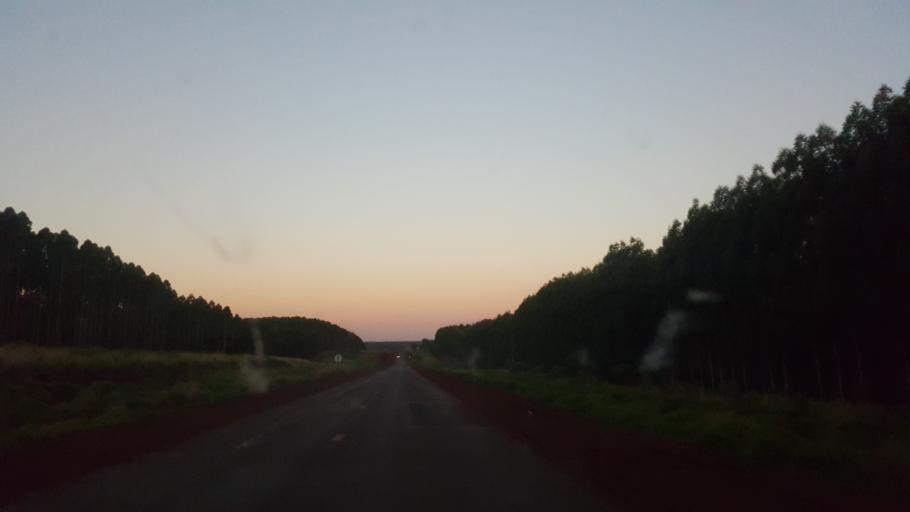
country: AR
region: Corrientes
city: Garruchos
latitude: -28.2463
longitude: -55.8398
